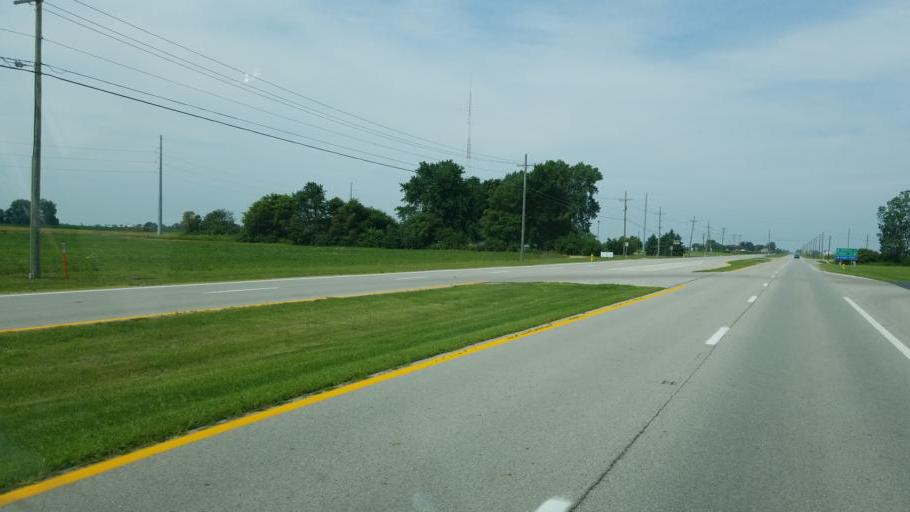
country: US
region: Ohio
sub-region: Madison County
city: West Jefferson
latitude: 39.9430
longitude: -83.3032
